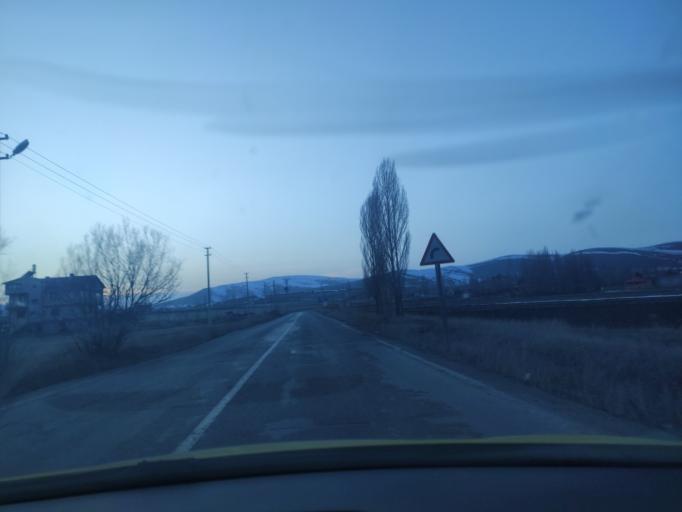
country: TR
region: Bayburt
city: Aydintepe
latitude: 40.3478
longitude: 40.1114
